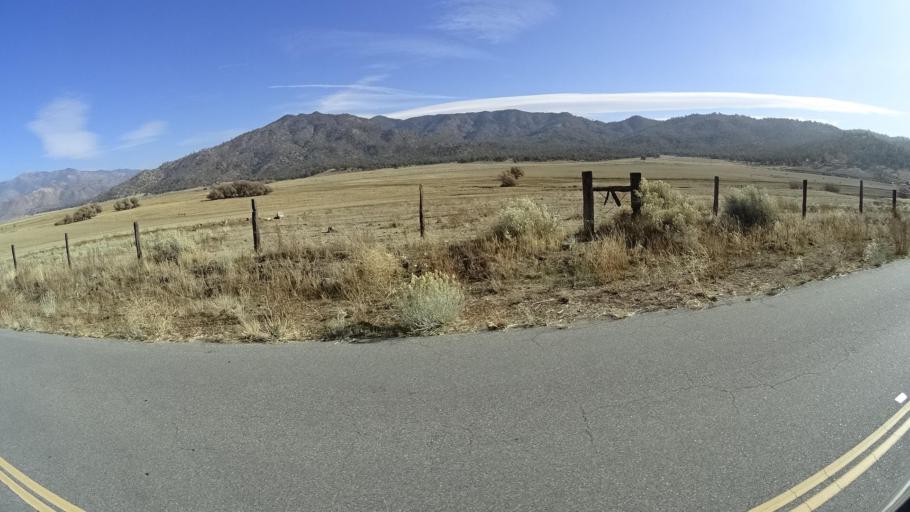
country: US
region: California
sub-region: Kern County
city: Bodfish
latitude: 35.3912
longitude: -118.5522
